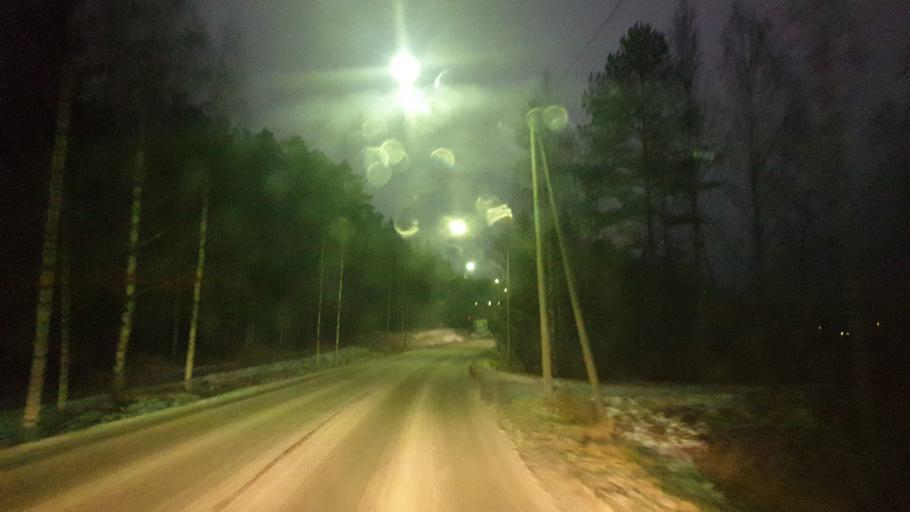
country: FI
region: Southern Savonia
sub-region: Savonlinna
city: Savonlinna
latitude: 61.8642
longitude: 28.9436
